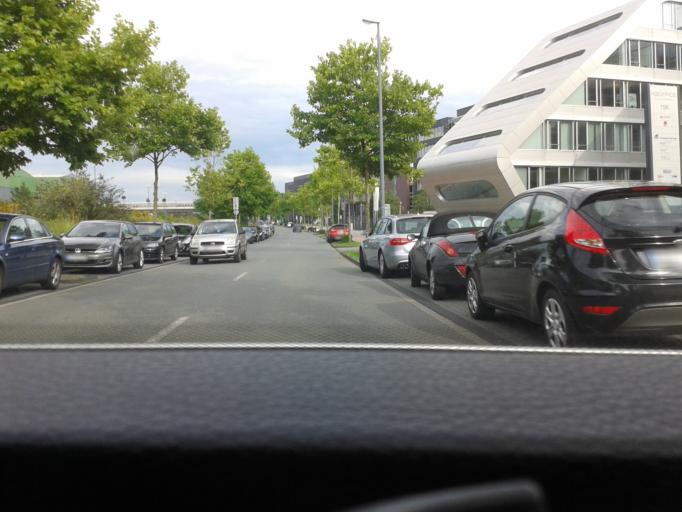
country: DE
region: North Rhine-Westphalia
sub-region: Regierungsbezirk Dusseldorf
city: Duisburg
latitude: 51.4427
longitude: 6.7705
